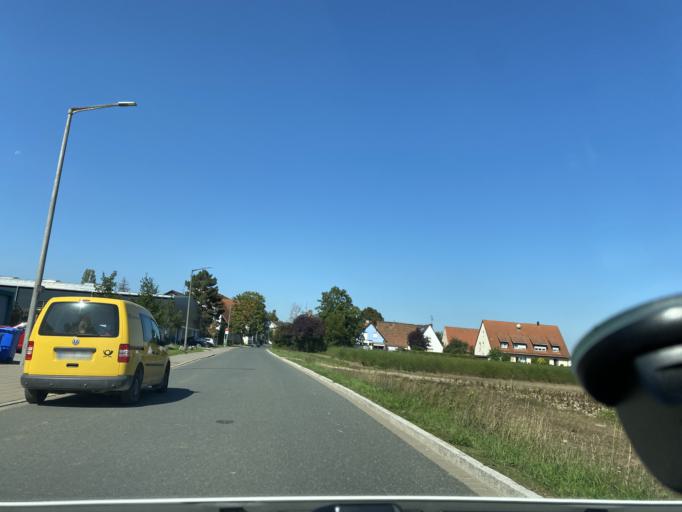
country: DE
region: Bavaria
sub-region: Regierungsbezirk Mittelfranken
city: Furth
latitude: 49.4991
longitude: 11.0011
